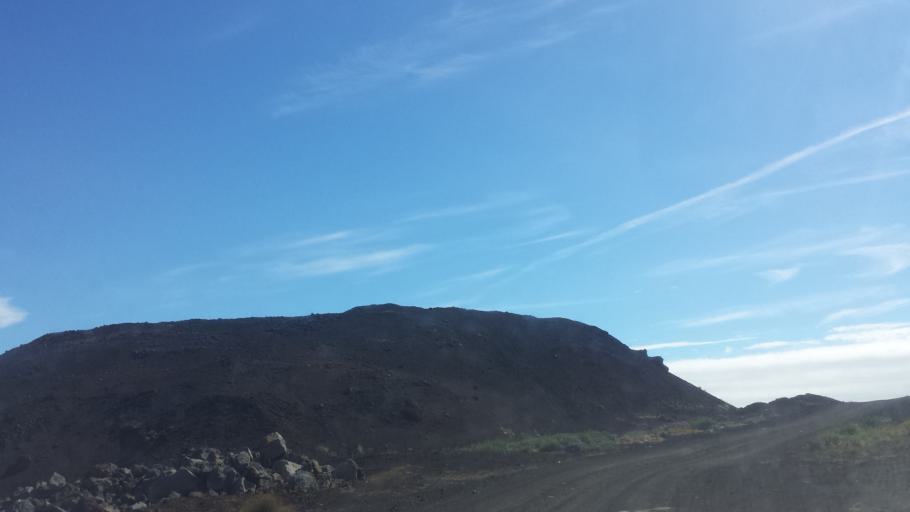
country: IS
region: South
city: Vestmannaeyjar
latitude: 63.4408
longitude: -20.2417
